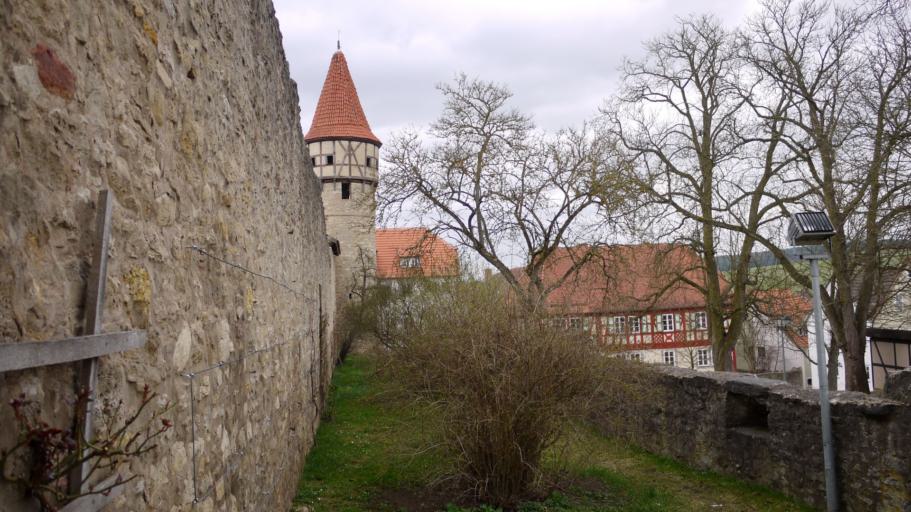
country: DE
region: Bavaria
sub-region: Regierungsbezirk Unterfranken
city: Ostheim vor der Rhon
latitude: 50.4592
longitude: 10.2312
